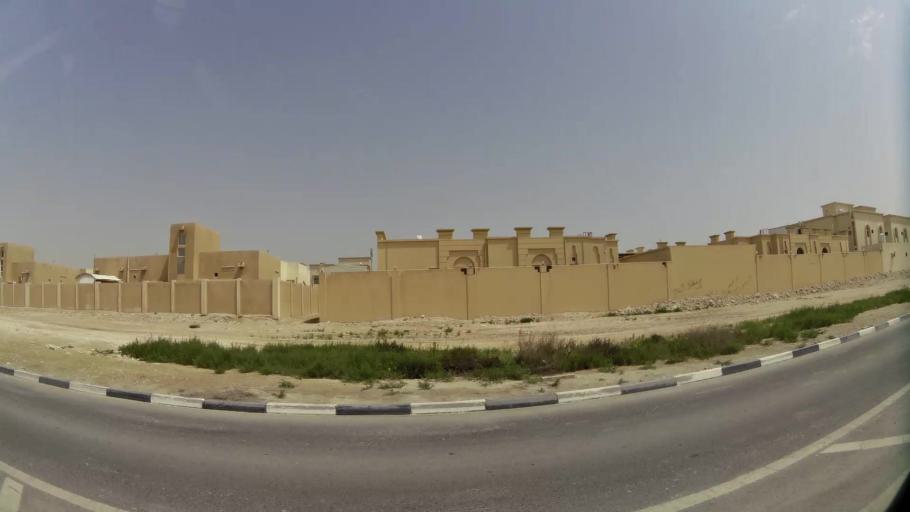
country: QA
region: Baladiyat ar Rayyan
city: Ar Rayyan
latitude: 25.2271
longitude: 51.4112
